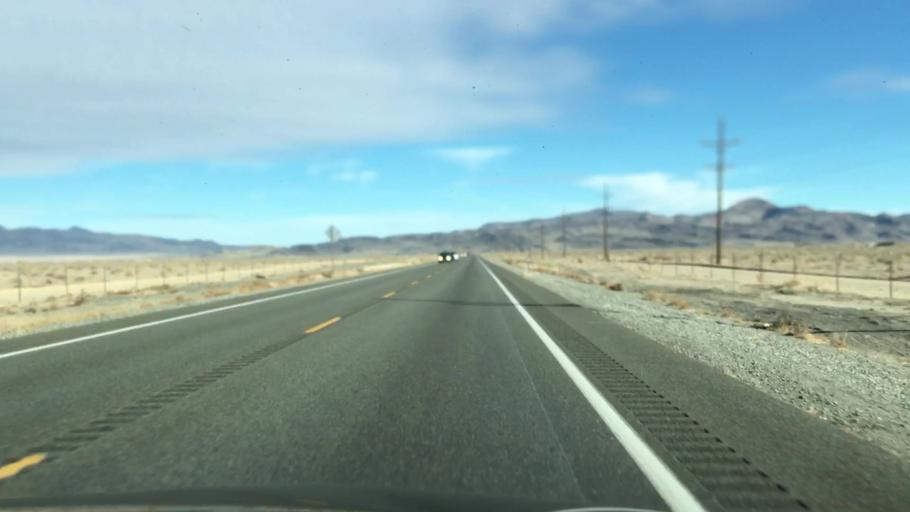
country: US
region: Nevada
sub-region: Mineral County
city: Hawthorne
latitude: 38.5246
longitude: -118.5880
